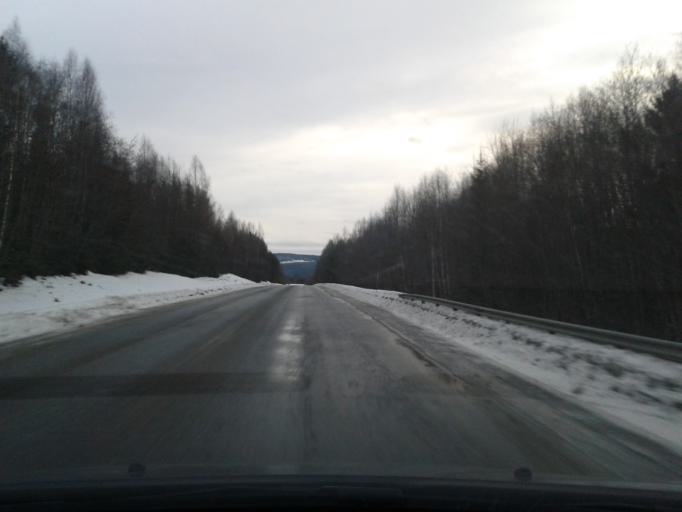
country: SE
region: Vaesternorrland
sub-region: Solleftea Kommun
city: Solleftea
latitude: 63.2787
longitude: 17.2162
